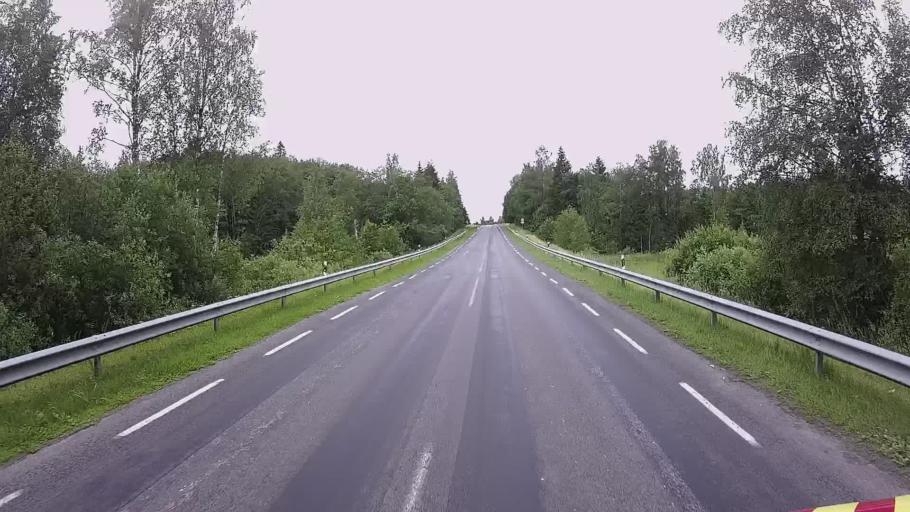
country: EE
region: Viljandimaa
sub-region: Karksi vald
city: Karksi-Nuia
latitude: 58.1858
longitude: 25.5979
